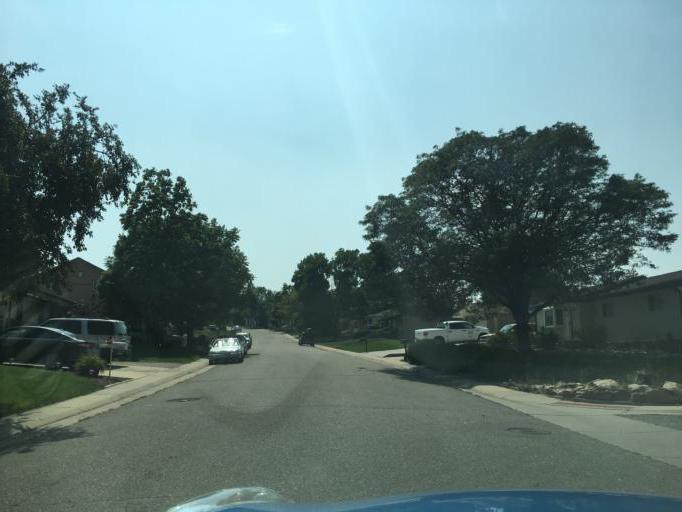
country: US
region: Colorado
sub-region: Adams County
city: Westminster
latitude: 39.8390
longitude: -105.0729
